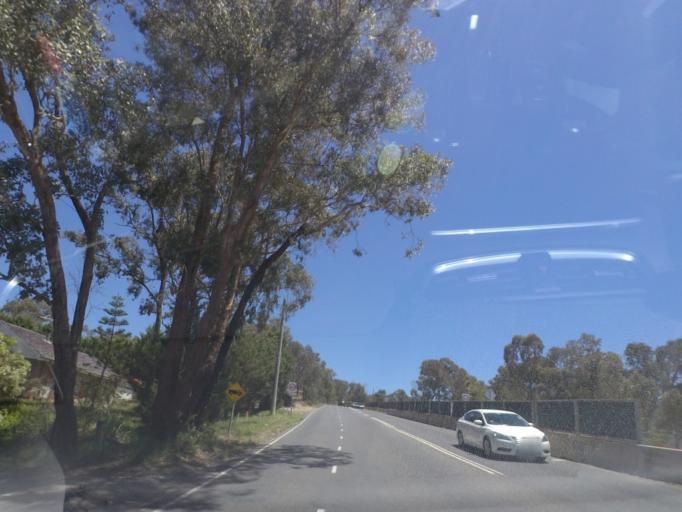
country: AU
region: Victoria
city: Plenty
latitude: -37.6545
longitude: 145.1230
